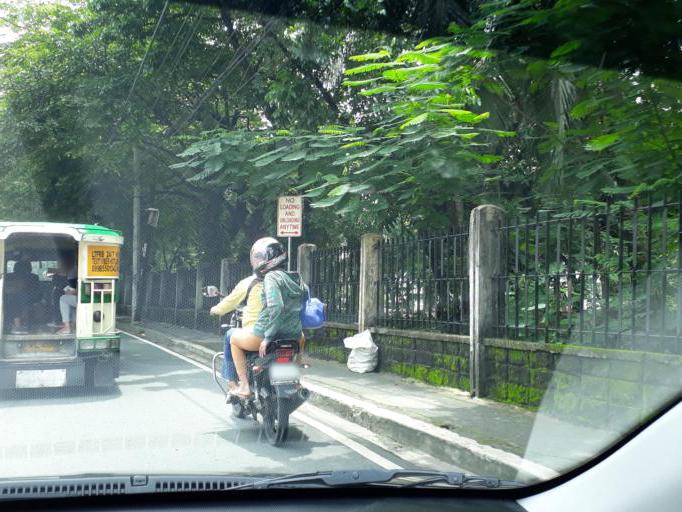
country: PH
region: Calabarzon
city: Del Monte
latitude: 14.6240
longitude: 121.0315
